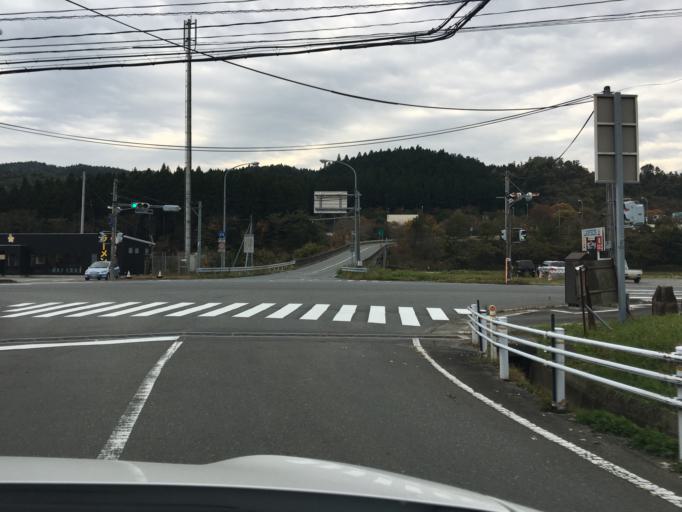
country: JP
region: Fukushima
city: Iwaki
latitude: 37.1018
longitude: 140.7738
